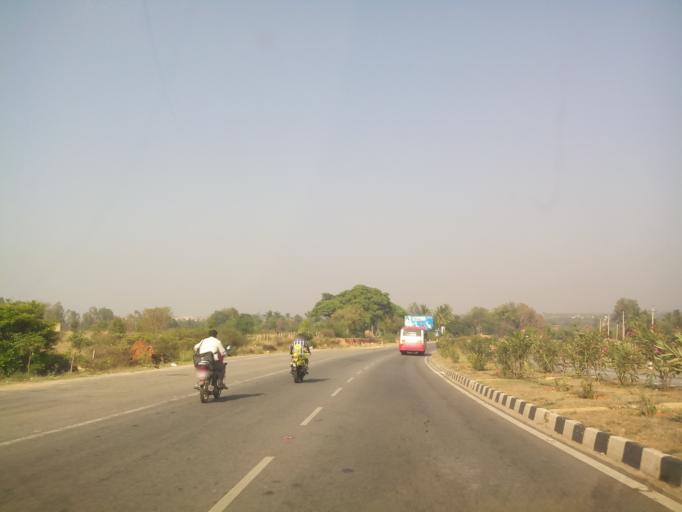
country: IN
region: Karnataka
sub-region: Bangalore Rural
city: Nelamangala
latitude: 13.0607
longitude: 77.3378
